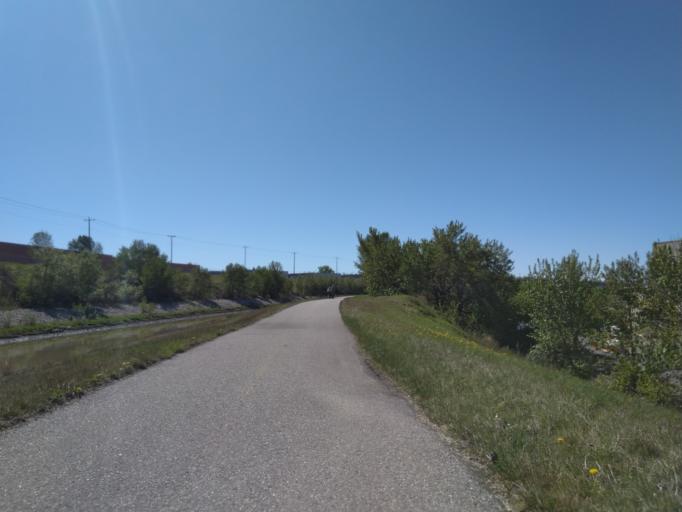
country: CA
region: Alberta
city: Calgary
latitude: 50.9940
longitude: -113.9871
